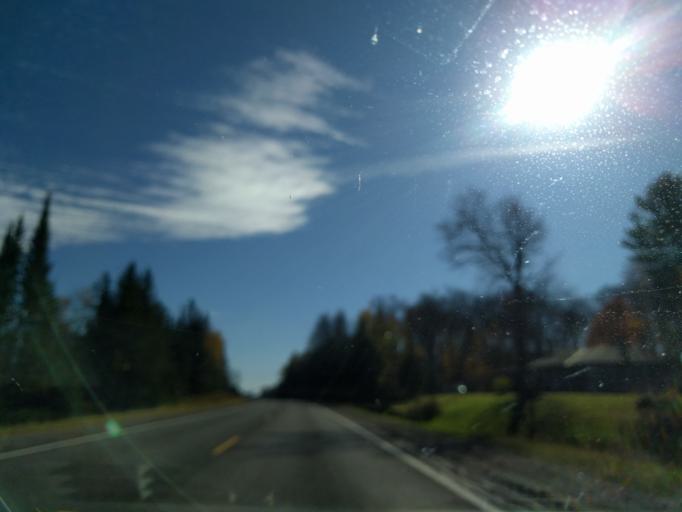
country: US
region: Michigan
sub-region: Marquette County
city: West Ishpeming
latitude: 46.3396
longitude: -87.9737
